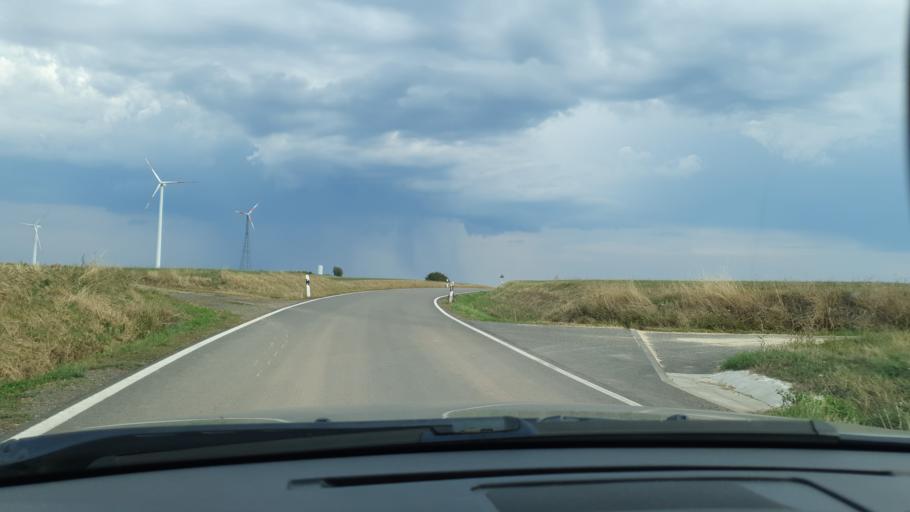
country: DE
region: Rheinland-Pfalz
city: Krahenberg
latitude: 49.3315
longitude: 7.4782
